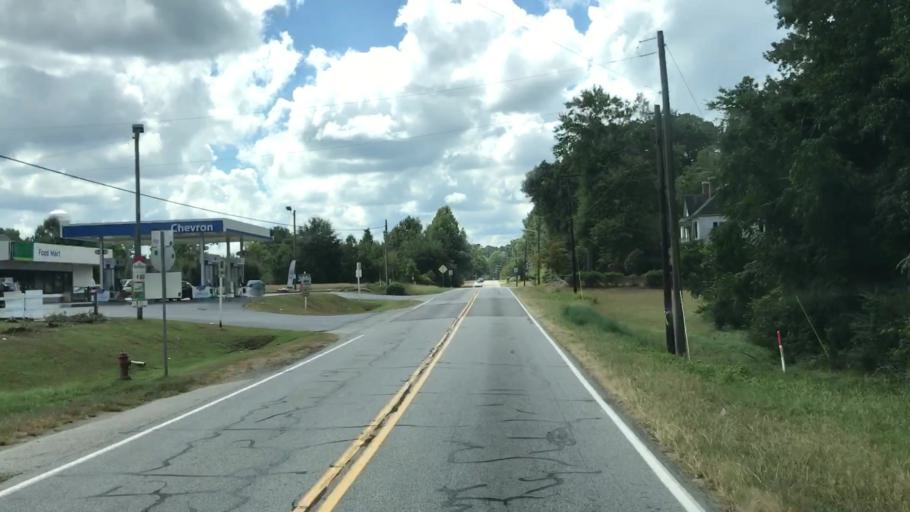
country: US
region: Georgia
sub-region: Greene County
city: Union Point
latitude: 33.5413
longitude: -83.0803
